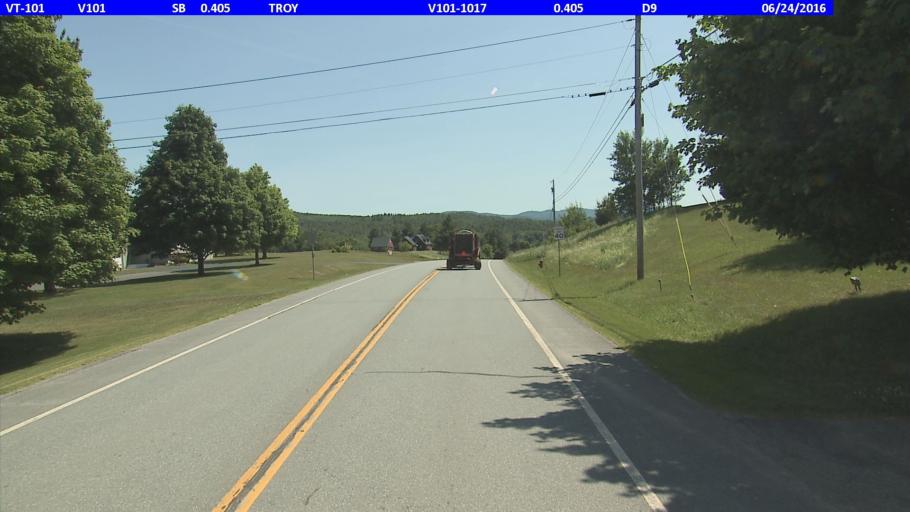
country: US
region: Vermont
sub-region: Orleans County
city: Newport
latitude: 44.9093
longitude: -72.4052
